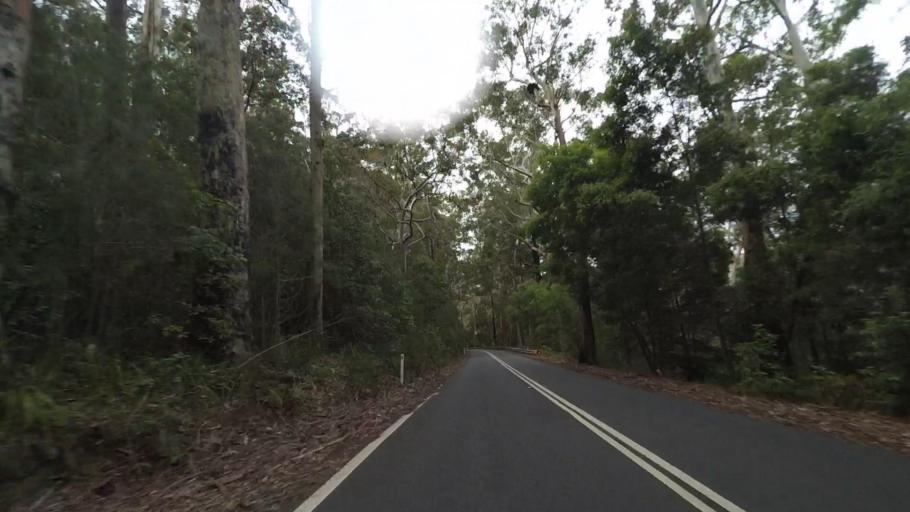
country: AU
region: New South Wales
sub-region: Wollongong
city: Helensburgh
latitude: -34.1548
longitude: 151.0320
